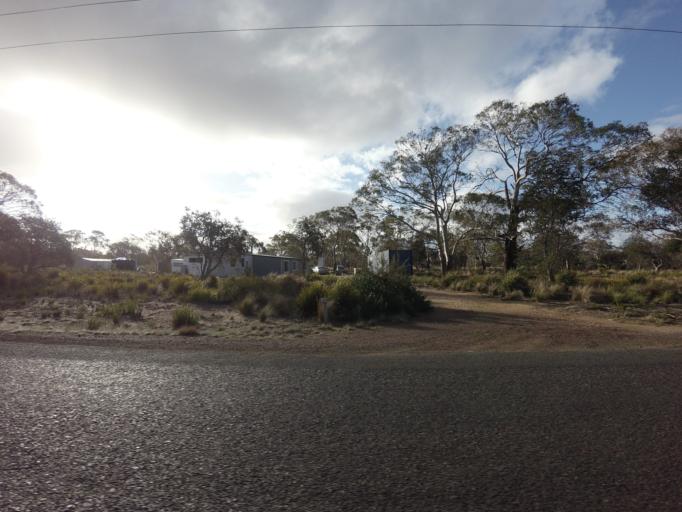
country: AU
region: Tasmania
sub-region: Break O'Day
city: St Helens
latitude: -42.0911
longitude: 148.1123
